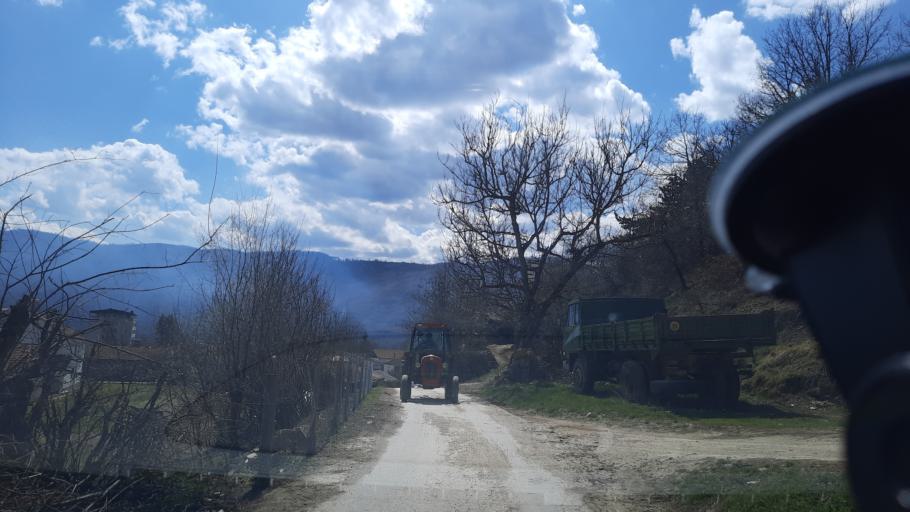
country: MK
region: Demir Hisar
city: Sopotnica
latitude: 41.2955
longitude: 21.1519
